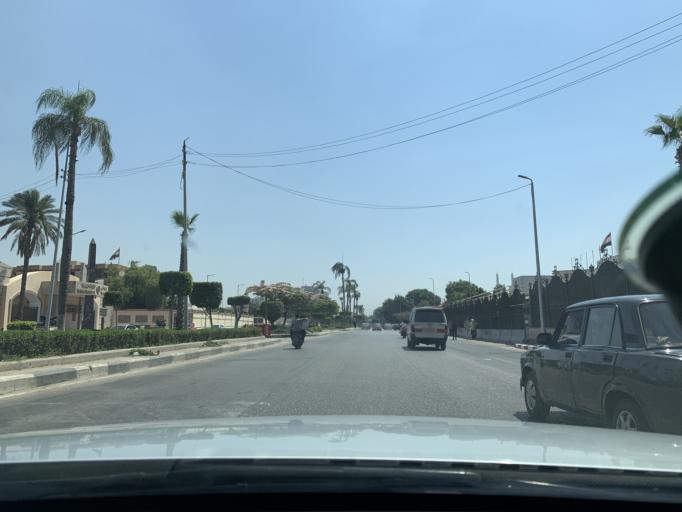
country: EG
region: Muhafazat al Qahirah
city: Cairo
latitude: 30.0806
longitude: 31.2920
